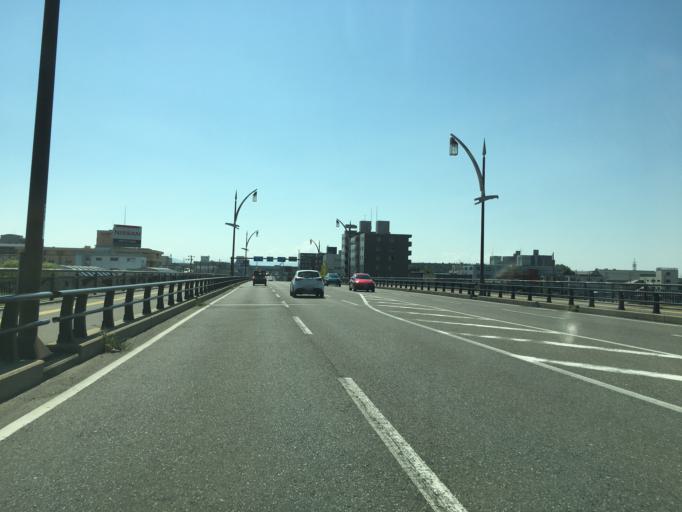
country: JP
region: Niigata
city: Niigata-shi
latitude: 37.9122
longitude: 139.0433
